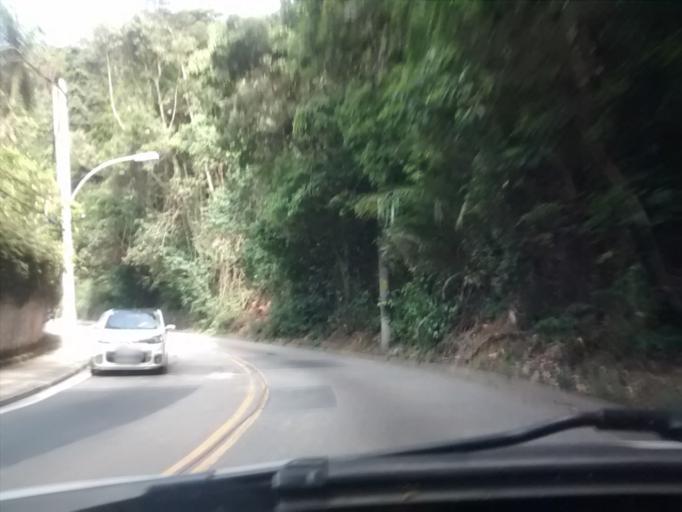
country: BR
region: Rio de Janeiro
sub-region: Rio De Janeiro
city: Rio de Janeiro
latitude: -22.9697
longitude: -43.2801
